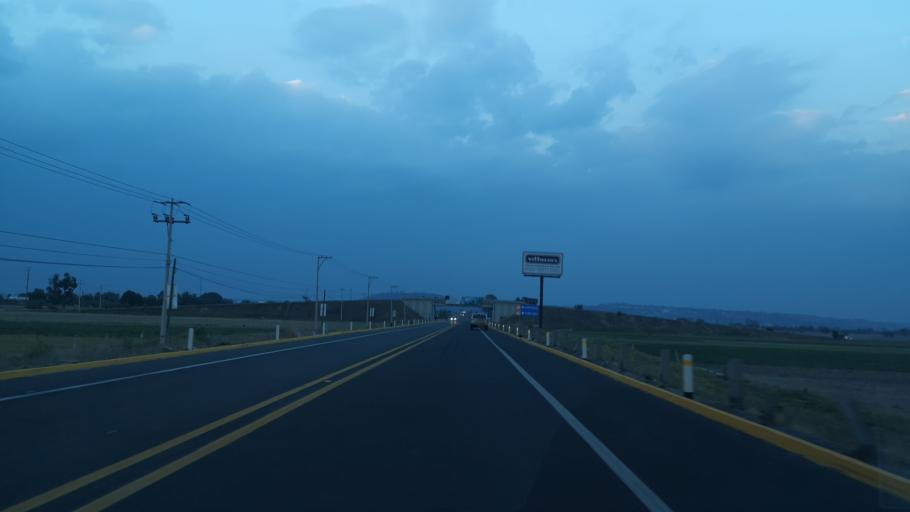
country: MX
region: Puebla
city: Santa Ana Xalmimilulco
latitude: 19.2002
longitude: -98.3637
